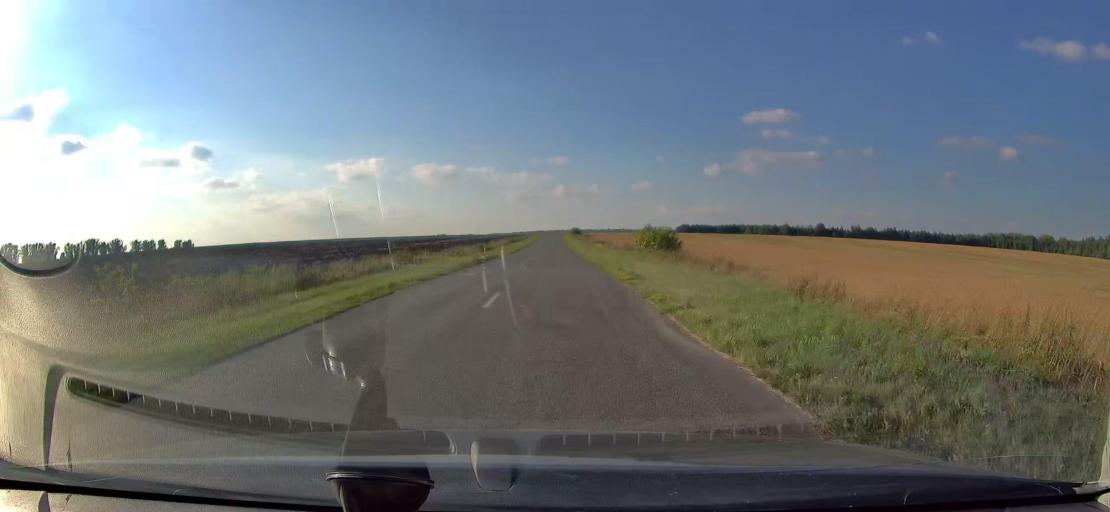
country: RU
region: Kursk
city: Zolotukhino
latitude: 52.0494
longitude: 36.2058
